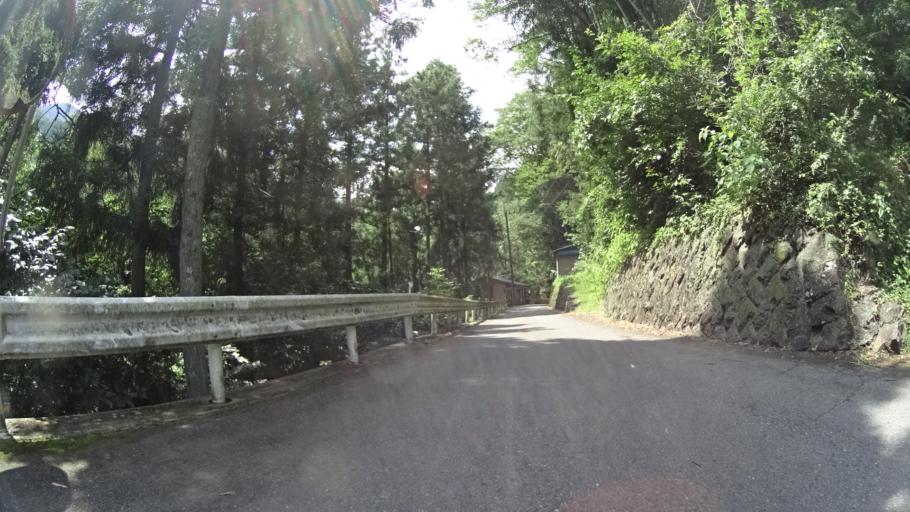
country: JP
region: Gunma
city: Tomioka
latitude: 36.0846
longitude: 138.7205
